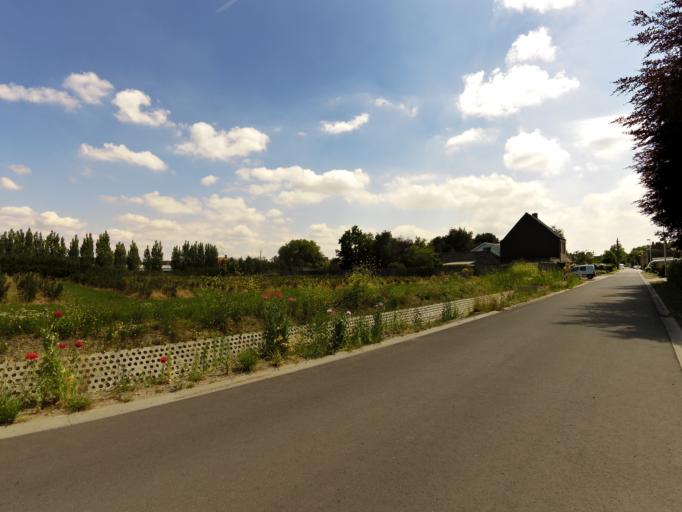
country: BE
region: Flanders
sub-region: Provincie West-Vlaanderen
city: Gistel
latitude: 51.1353
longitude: 2.9841
